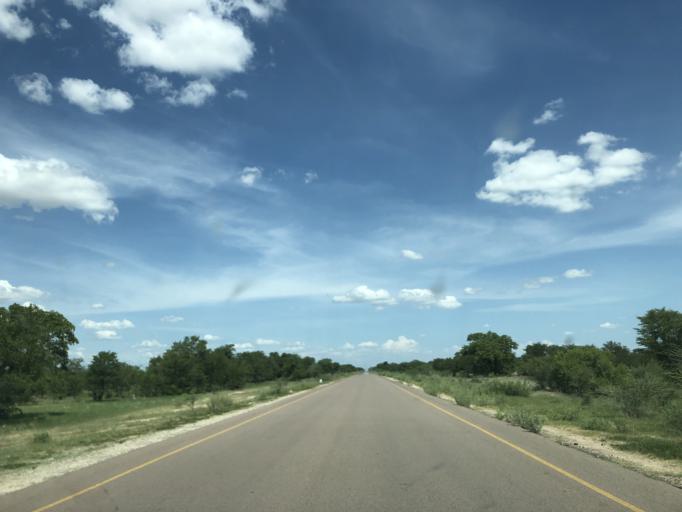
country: AO
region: Cunene
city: Ondjiva
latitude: -16.9040
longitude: 15.5159
